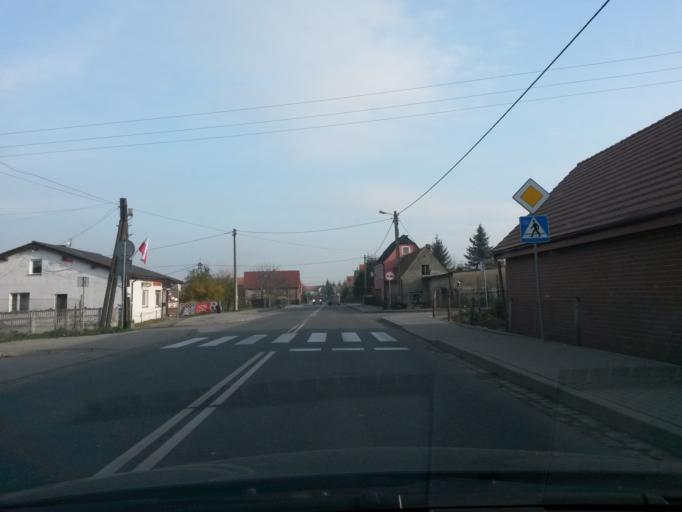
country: PL
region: Lower Silesian Voivodeship
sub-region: Powiat sredzki
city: Udanin
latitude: 50.9873
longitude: 16.4250
